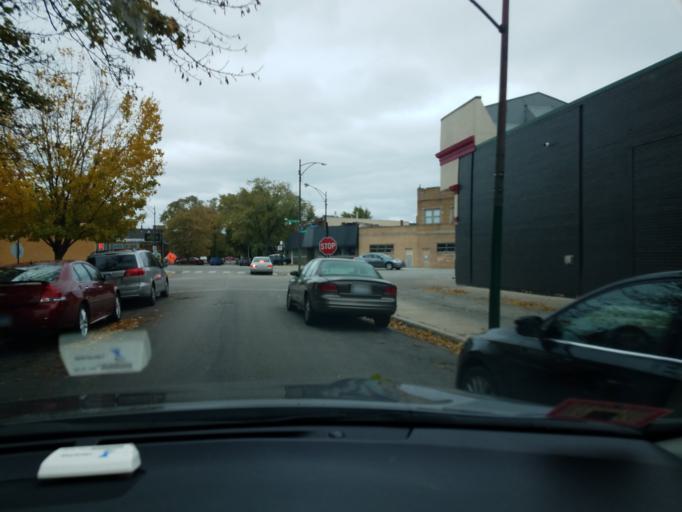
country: US
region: Illinois
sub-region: Cook County
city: Lincolnwood
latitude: 41.9559
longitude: -87.7216
